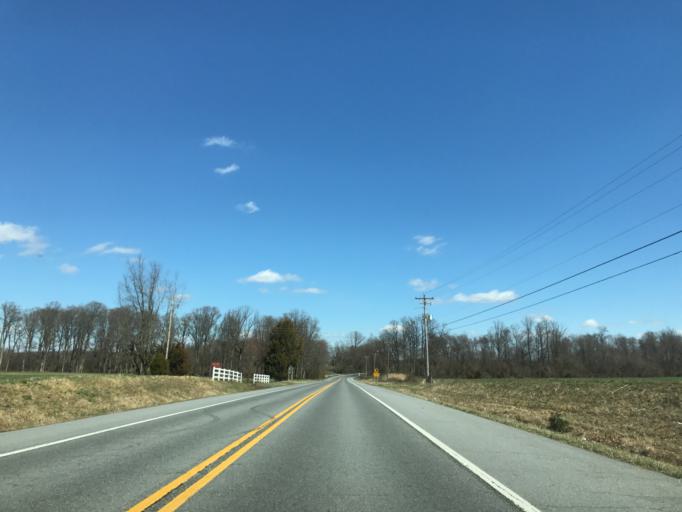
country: US
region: Maryland
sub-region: Queen Anne's County
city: Kingstown
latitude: 39.2420
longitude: -75.8823
